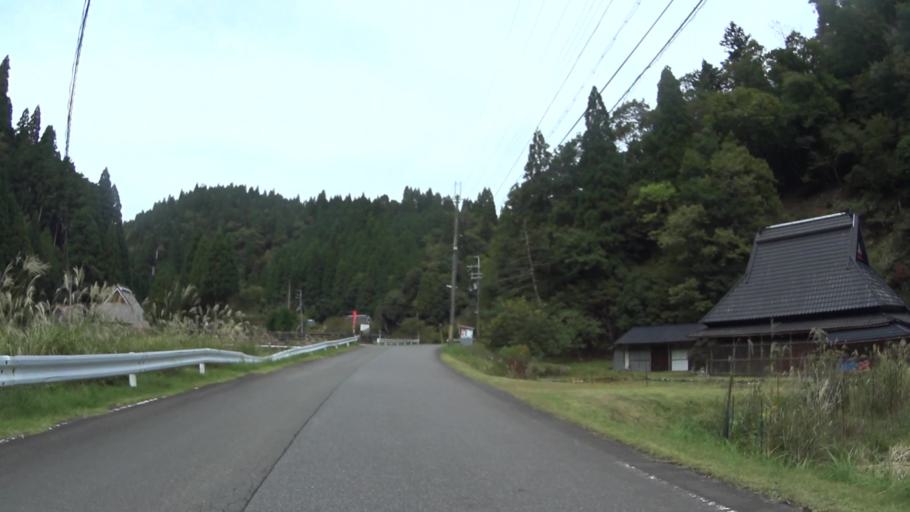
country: JP
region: Shiga Prefecture
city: Kitahama
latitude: 35.2584
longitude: 135.7522
